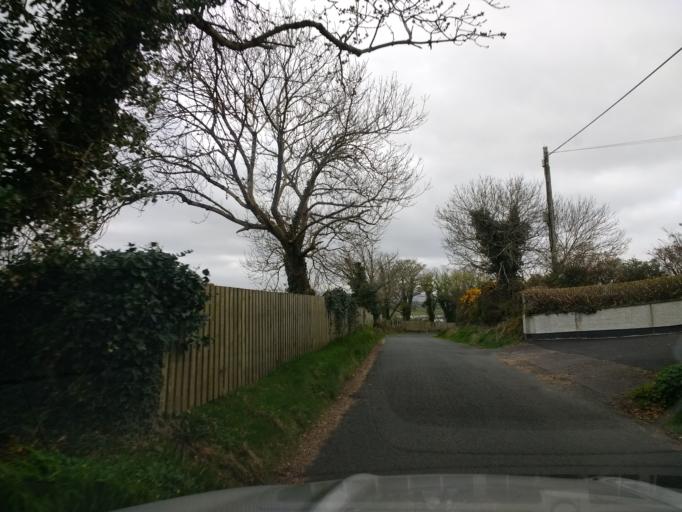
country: IE
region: Ulster
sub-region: County Donegal
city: Ramelton
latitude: 55.2110
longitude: -7.6176
